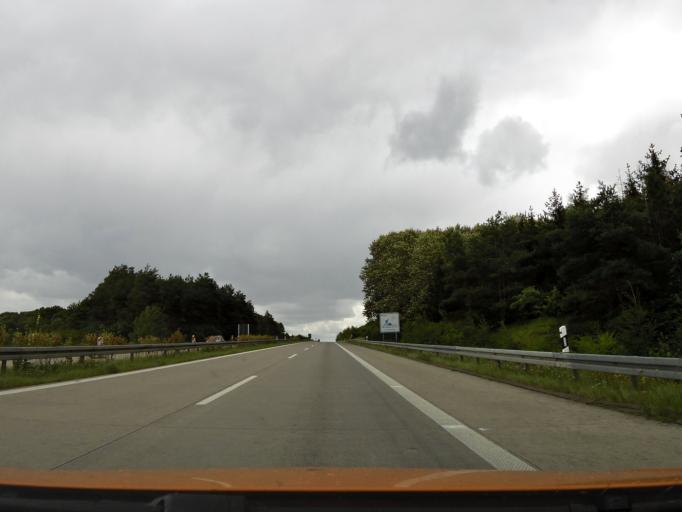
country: DE
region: Mecklenburg-Vorpommern
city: Penkun
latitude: 53.2952
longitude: 14.1331
